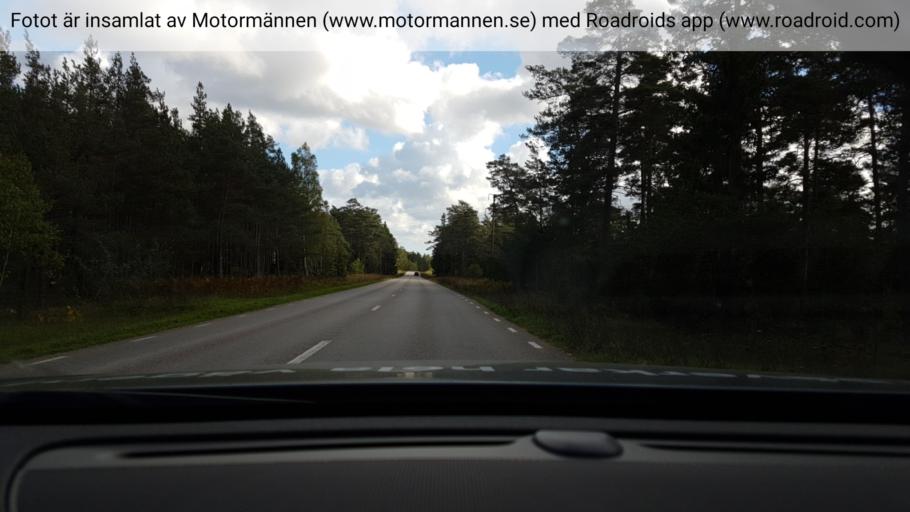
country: SE
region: Gotland
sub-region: Gotland
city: Hemse
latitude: 57.4605
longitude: 18.5734
